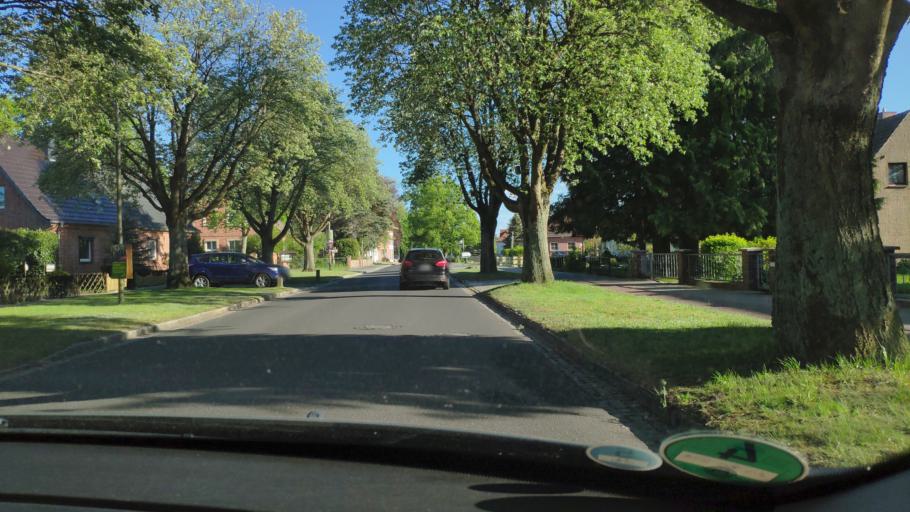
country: DE
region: Mecklenburg-Vorpommern
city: Rechlin
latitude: 53.2799
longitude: 12.8151
